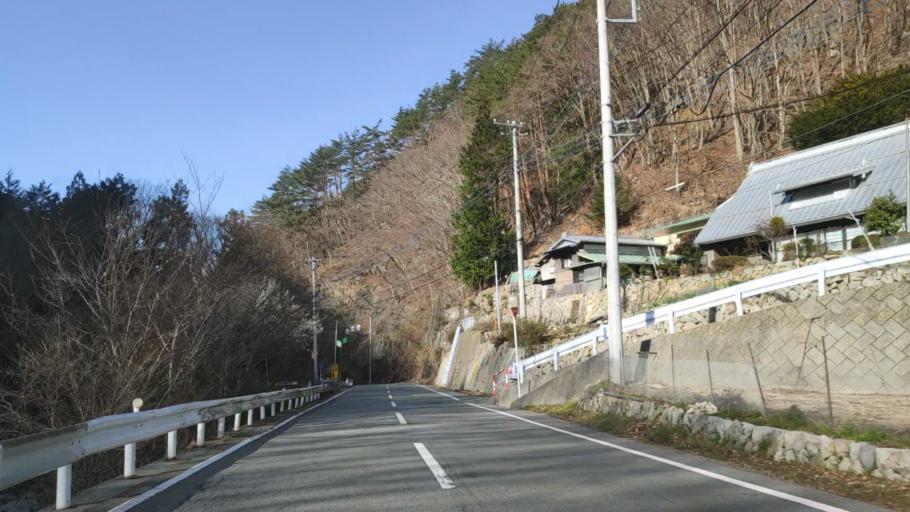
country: JP
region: Yamanashi
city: Fujikawaguchiko
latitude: 35.5530
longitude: 138.6628
